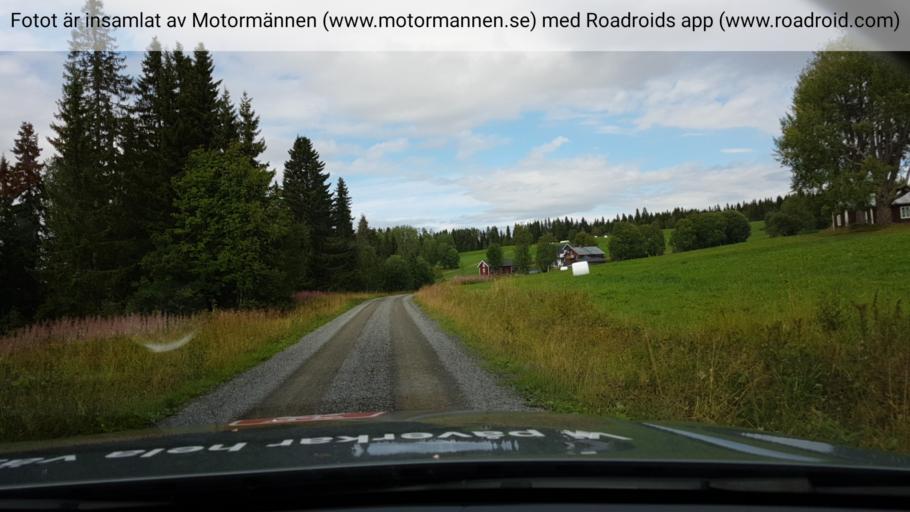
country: SE
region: Jaemtland
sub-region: Krokoms Kommun
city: Valla
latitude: 63.5243
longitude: 13.8869
